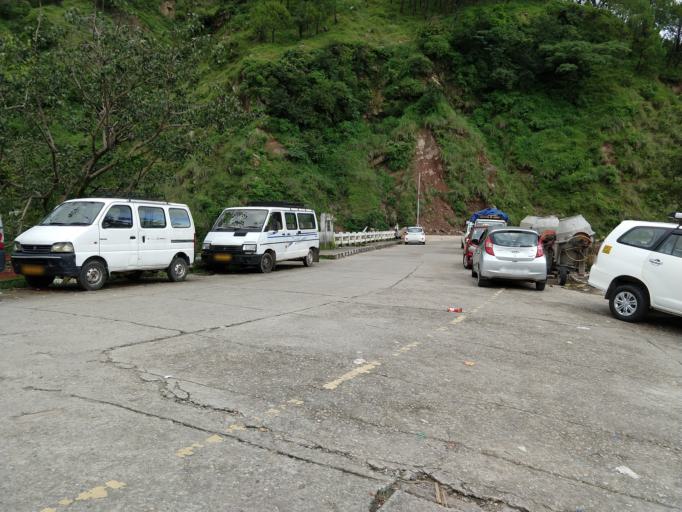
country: IN
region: Himachal Pradesh
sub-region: Kangra
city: Dharmsala
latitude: 32.2213
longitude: 76.3291
